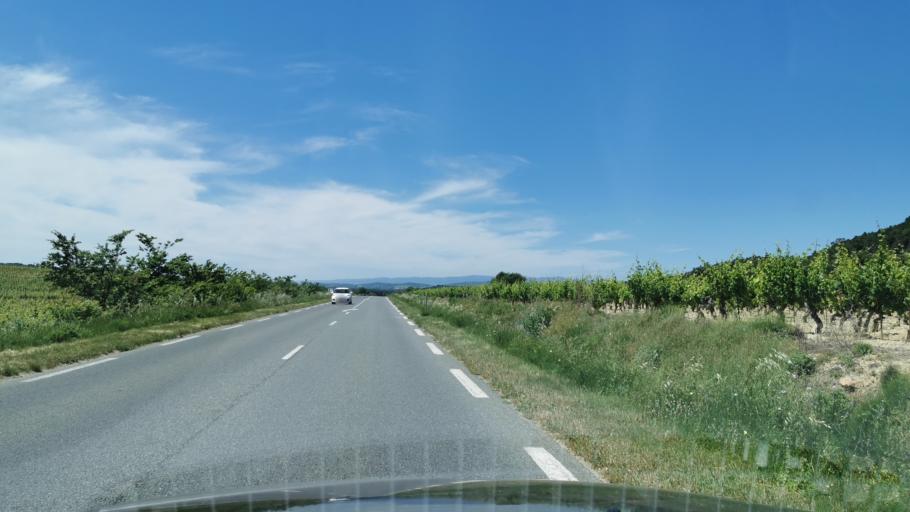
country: FR
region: Languedoc-Roussillon
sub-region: Departement de l'Aude
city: Moussan
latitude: 43.2091
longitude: 2.9489
